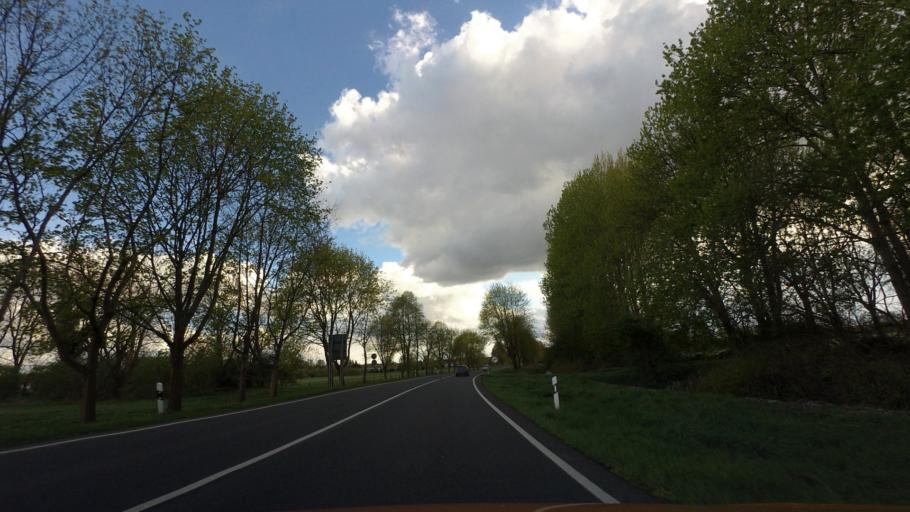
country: DE
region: Brandenburg
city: Friesack
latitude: 52.7472
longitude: 12.5753
